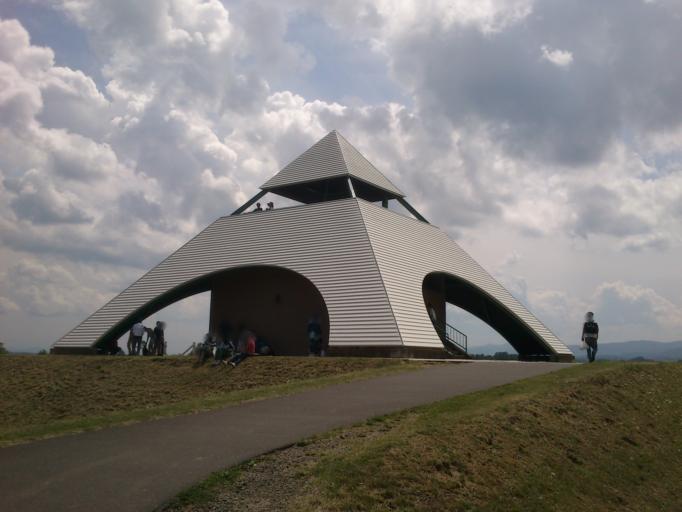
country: JP
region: Hokkaido
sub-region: Asahikawa-shi
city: Asahikawa
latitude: 43.6055
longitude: 142.4567
